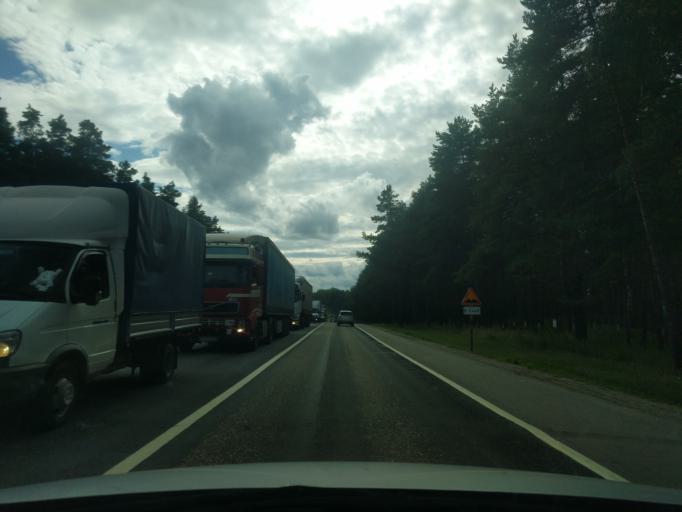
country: RU
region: Jaroslavl
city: Levashevo
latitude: 57.6750
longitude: 40.5867
